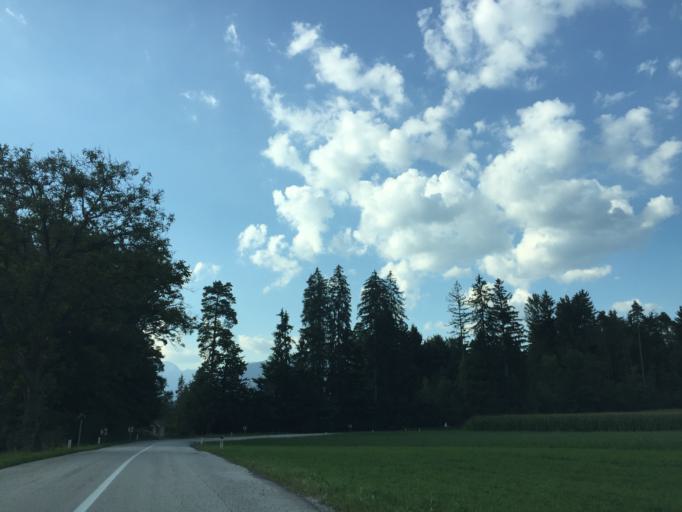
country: SI
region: Trzic
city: Bistrica pri Trzicu
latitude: 46.3034
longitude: 14.2651
